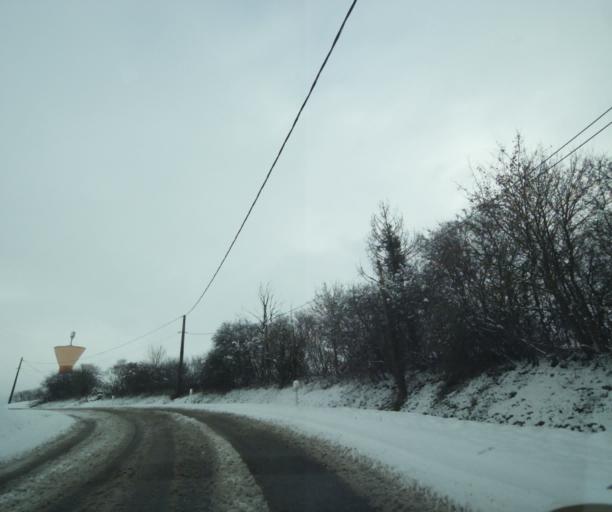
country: FR
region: Champagne-Ardenne
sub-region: Departement de la Haute-Marne
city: Montier-en-Der
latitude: 48.5100
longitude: 4.7030
